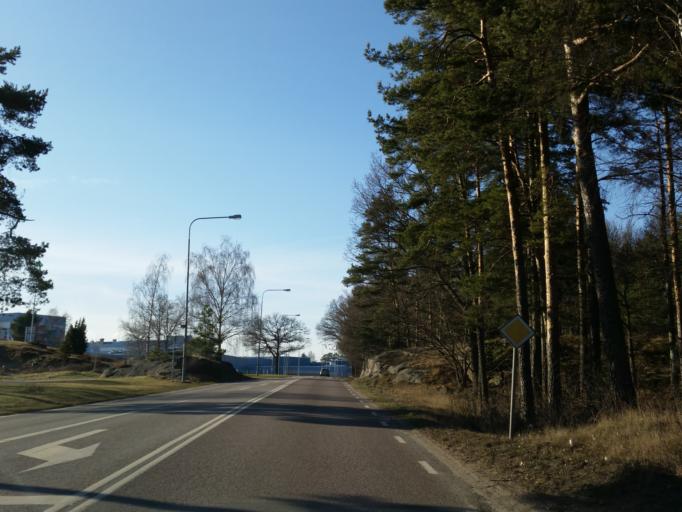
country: SE
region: Kalmar
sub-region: Oskarshamns Kommun
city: Oskarshamn
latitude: 57.2560
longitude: 16.4368
